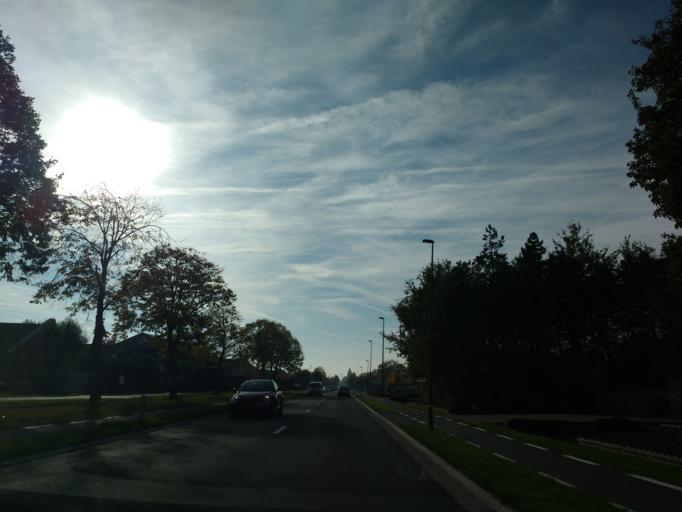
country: BE
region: Flanders
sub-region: Provincie Oost-Vlaanderen
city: Kaprijke
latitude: 51.2272
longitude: 3.6193
